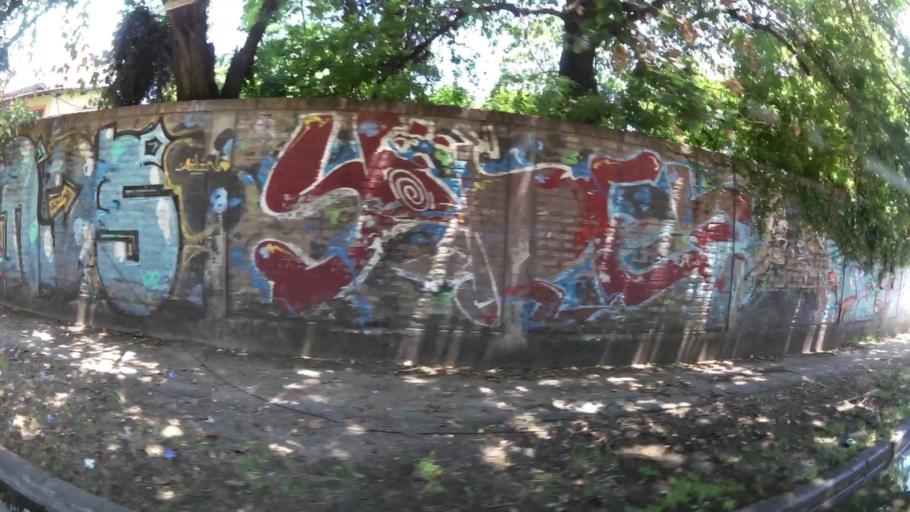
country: AR
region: Buenos Aires
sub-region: Partido de Merlo
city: Merlo
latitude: -34.6626
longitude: -58.7043
